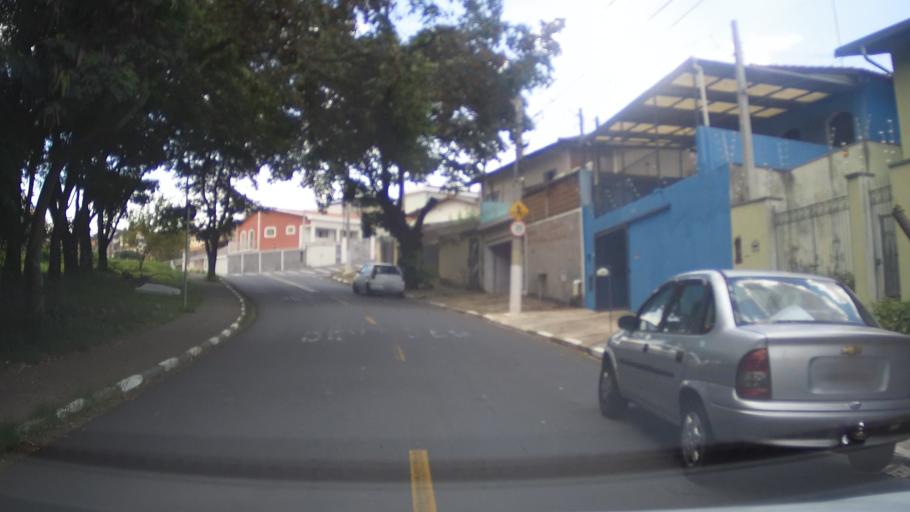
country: BR
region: Sao Paulo
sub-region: Campinas
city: Campinas
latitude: -22.9199
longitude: -47.0371
